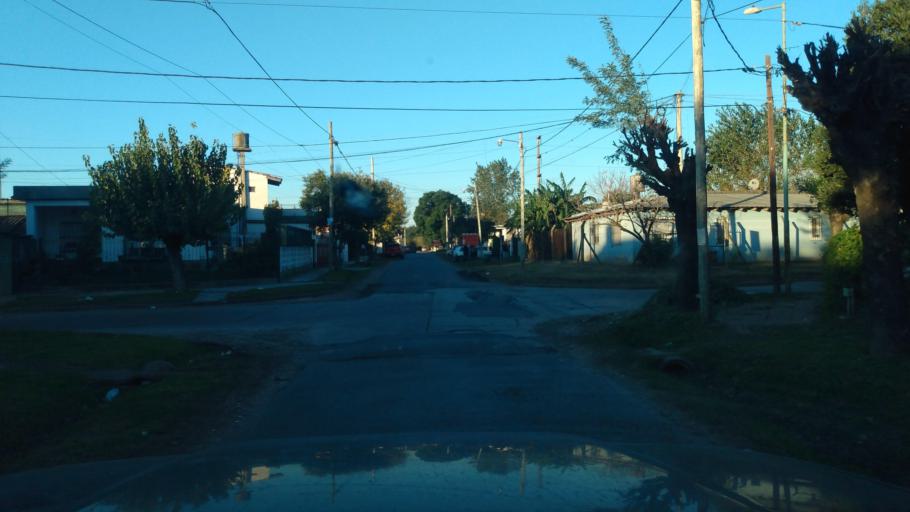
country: AR
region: Buenos Aires
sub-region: Partido de Merlo
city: Merlo
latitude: -34.6572
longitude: -58.7477
